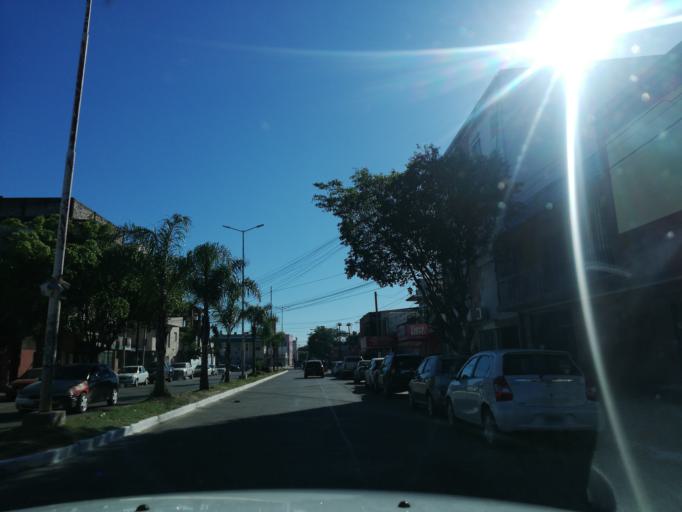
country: AR
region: Corrientes
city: Corrientes
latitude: -27.4721
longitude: -58.8129
